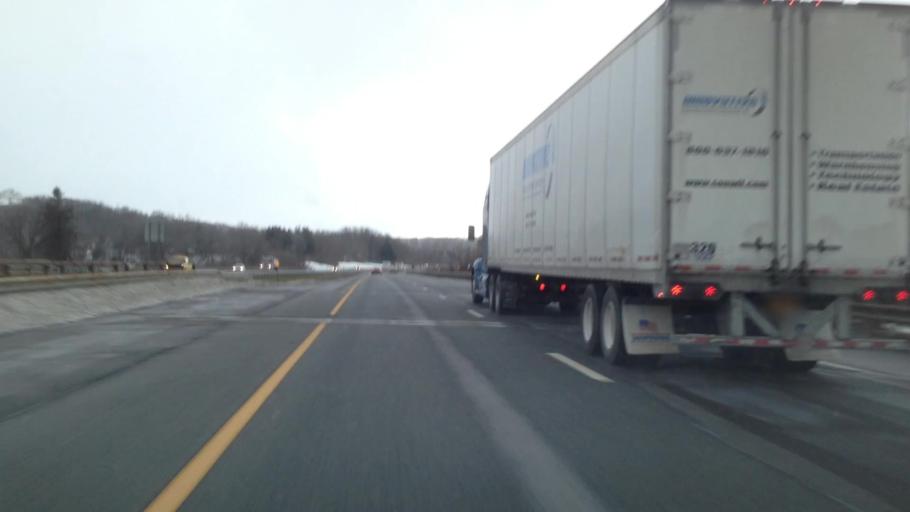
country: US
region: New York
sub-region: Herkimer County
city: Little Falls
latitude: 43.0063
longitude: -74.7777
